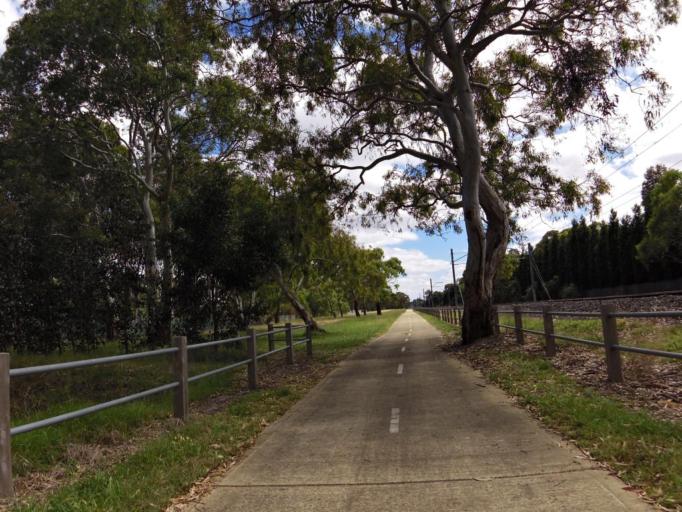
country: AU
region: Victoria
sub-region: Moreland
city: Fawkner
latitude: -37.7107
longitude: 144.9599
